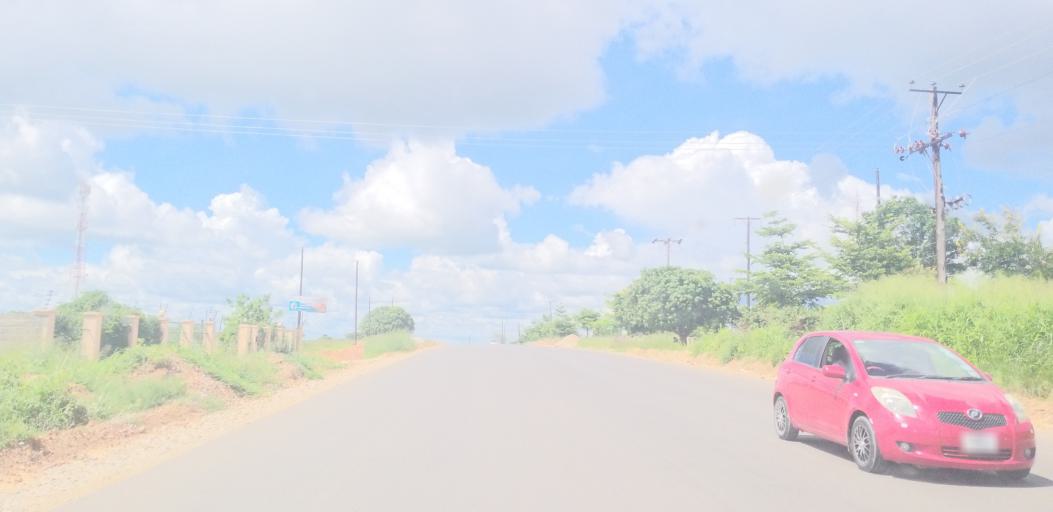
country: ZM
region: Lusaka
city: Lusaka
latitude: -15.3517
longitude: 28.3252
